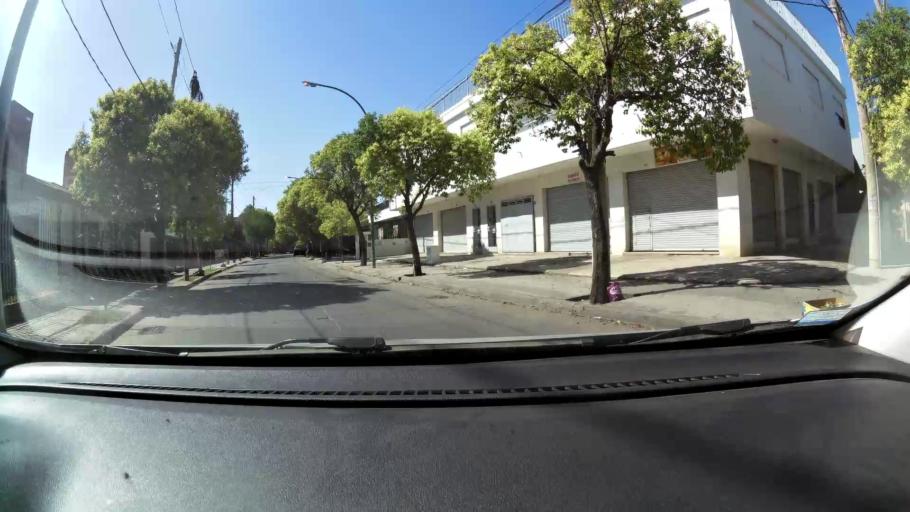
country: AR
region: Cordoba
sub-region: Departamento de Capital
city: Cordoba
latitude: -31.3795
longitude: -64.1710
